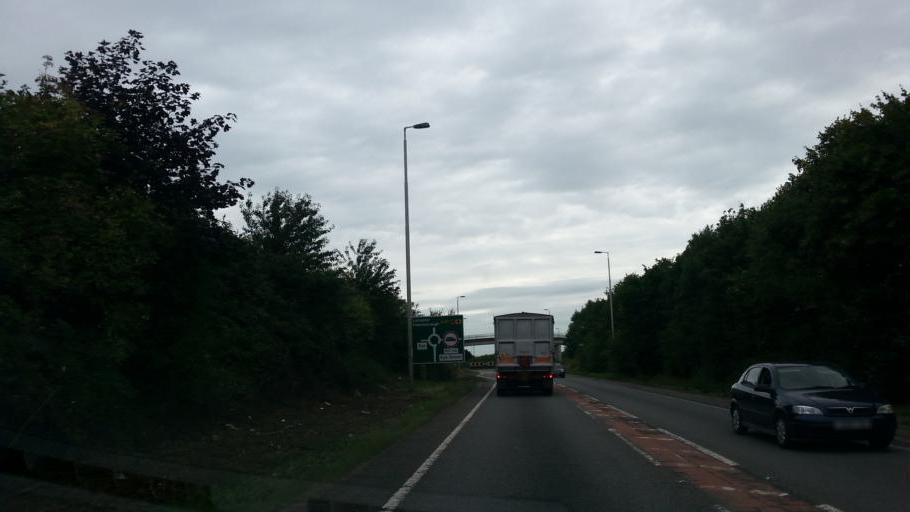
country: GB
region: England
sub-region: Peterborough
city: Eye
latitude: 52.6126
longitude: -0.1824
